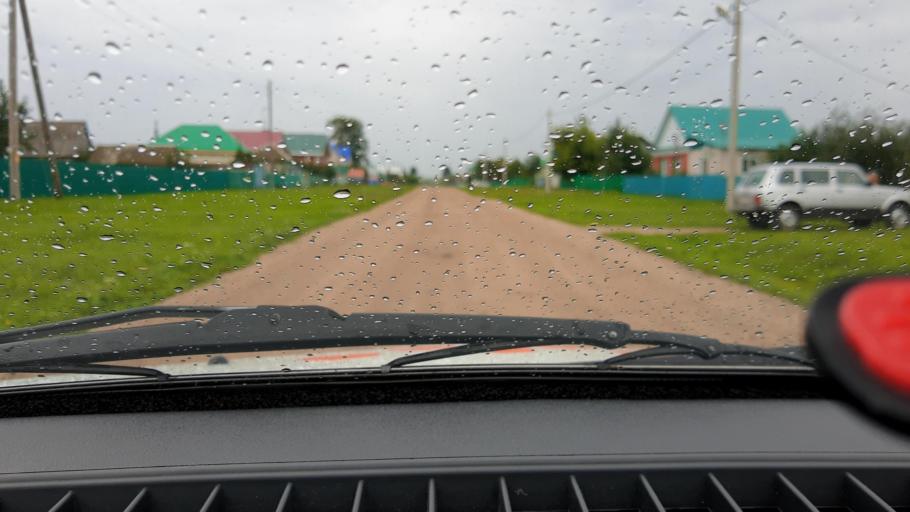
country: RU
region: Bashkortostan
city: Karmaskaly
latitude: 54.3809
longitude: 56.1142
